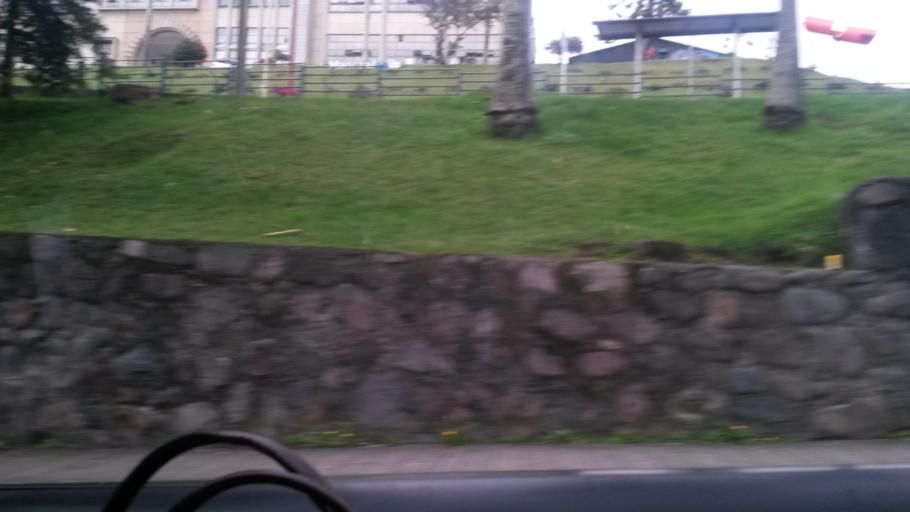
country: CO
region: Caldas
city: Manizales
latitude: 5.0675
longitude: -75.5231
